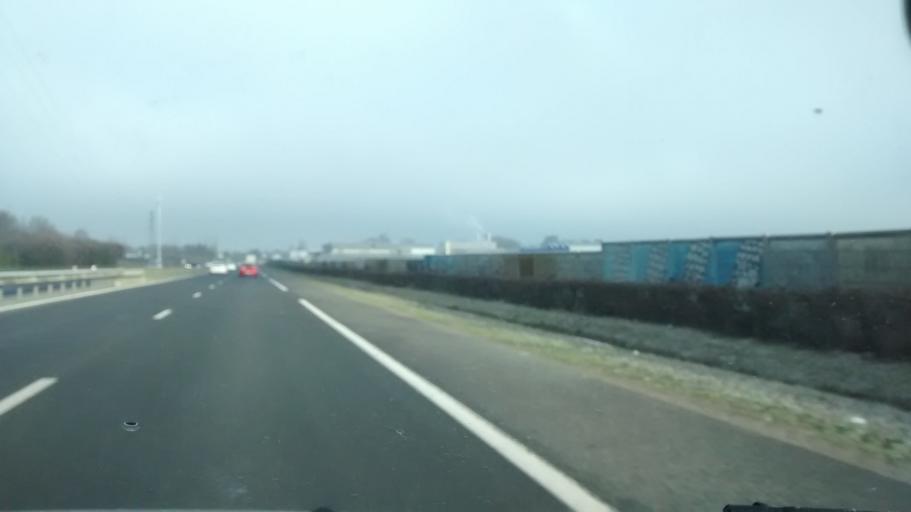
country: FR
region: Centre
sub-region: Departement d'Indre-et-Loire
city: Joue-les-Tours
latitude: 47.3518
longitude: 0.6461
